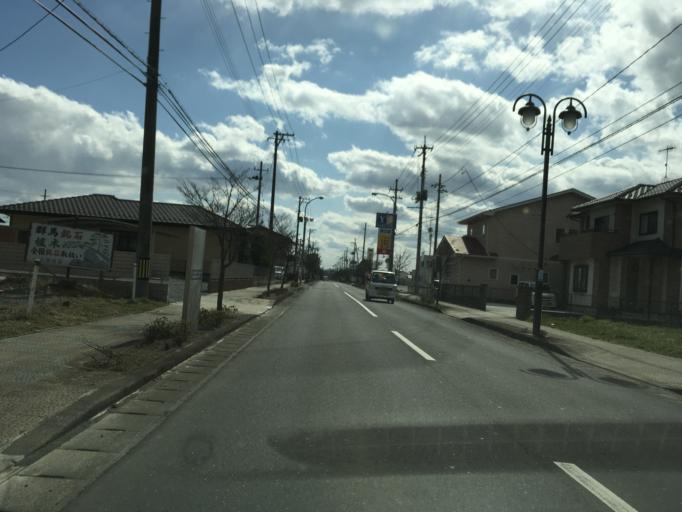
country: JP
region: Miyagi
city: Wakuya
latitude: 38.7017
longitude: 141.2120
